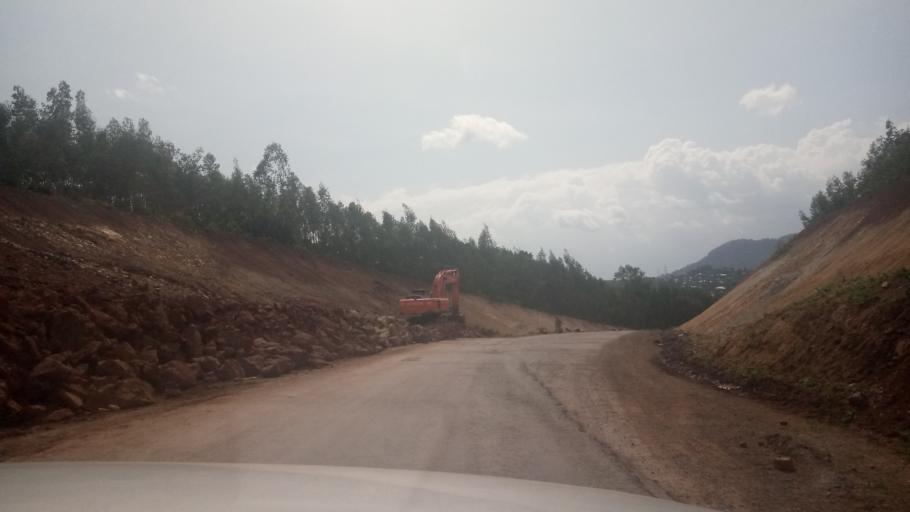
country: ET
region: Oromiya
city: Agaro
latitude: 7.9916
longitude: 36.5053
